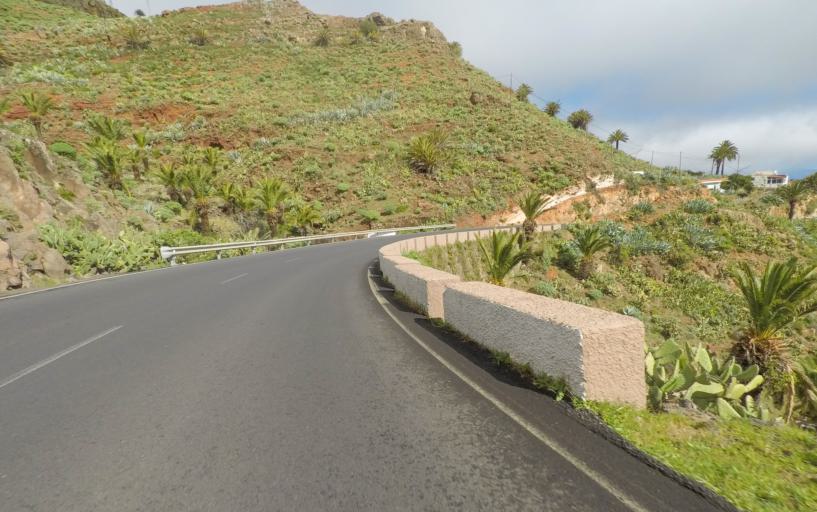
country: ES
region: Canary Islands
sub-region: Provincia de Santa Cruz de Tenerife
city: San Sebastian de la Gomera
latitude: 28.0984
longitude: -17.1736
